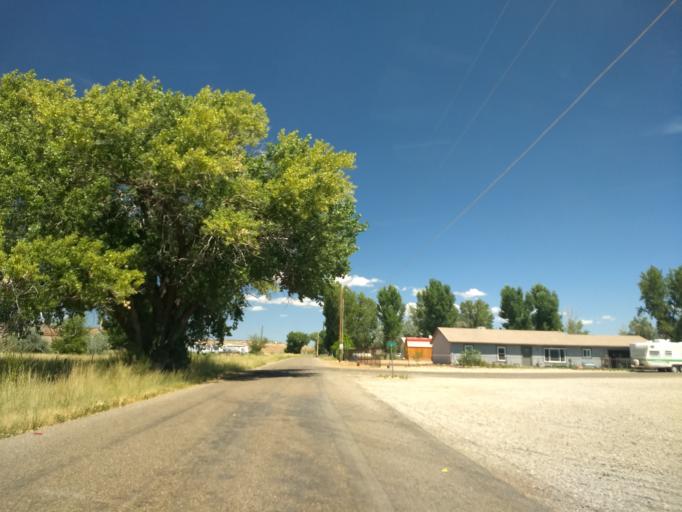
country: US
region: Arizona
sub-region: Coconino County
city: Fredonia
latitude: 36.9407
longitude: -112.5353
